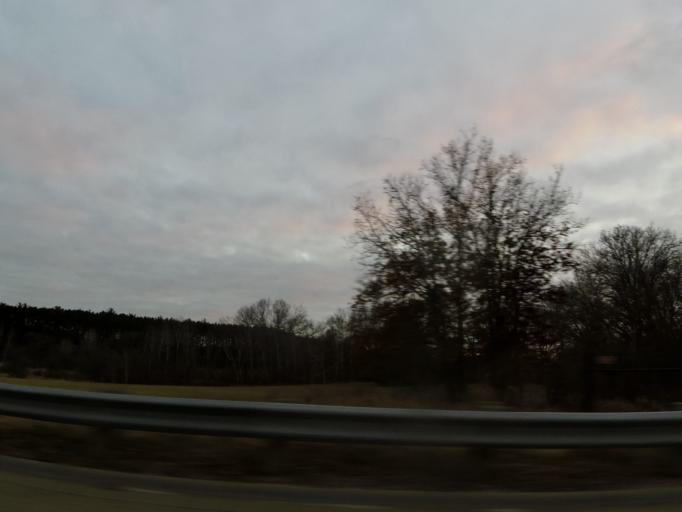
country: US
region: Minnesota
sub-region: Washington County
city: Mahtomedi
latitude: 45.0576
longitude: -92.9283
